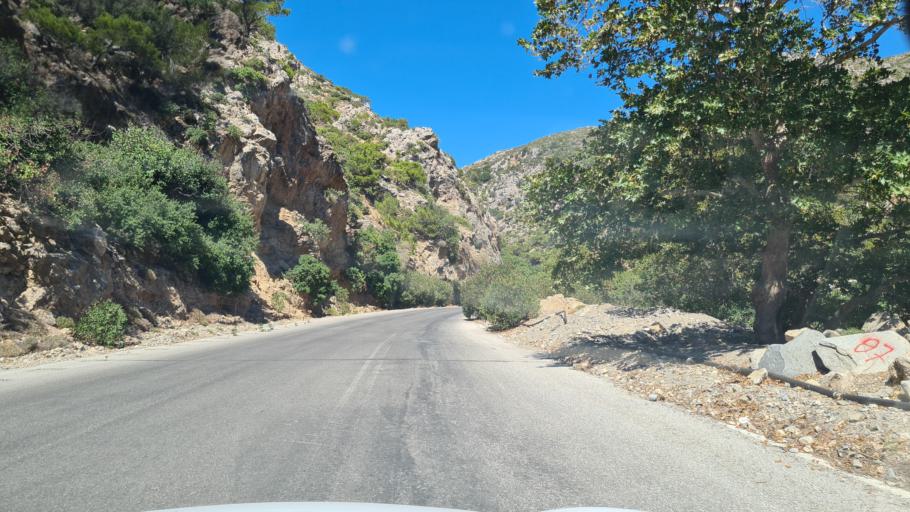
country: GR
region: Crete
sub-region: Nomos Chanias
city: Vryses
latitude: 35.3394
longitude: 23.5761
